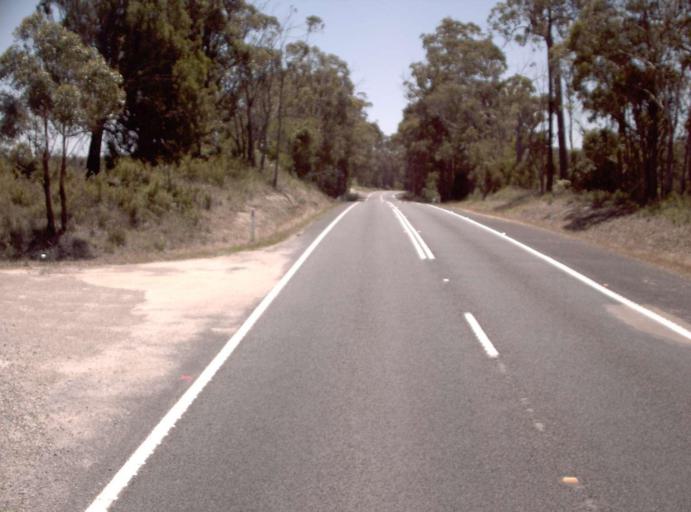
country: AU
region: Victoria
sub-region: East Gippsland
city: Lakes Entrance
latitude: -37.8355
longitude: 148.0318
